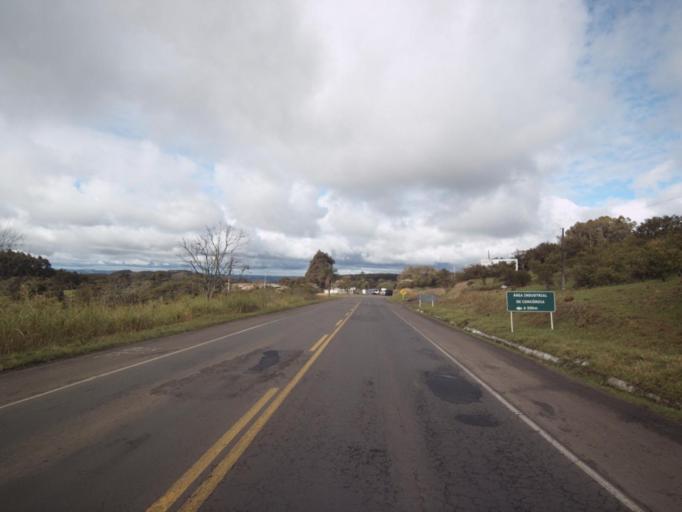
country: BR
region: Santa Catarina
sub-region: Concordia
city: Concordia
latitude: -27.2101
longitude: -51.9517
